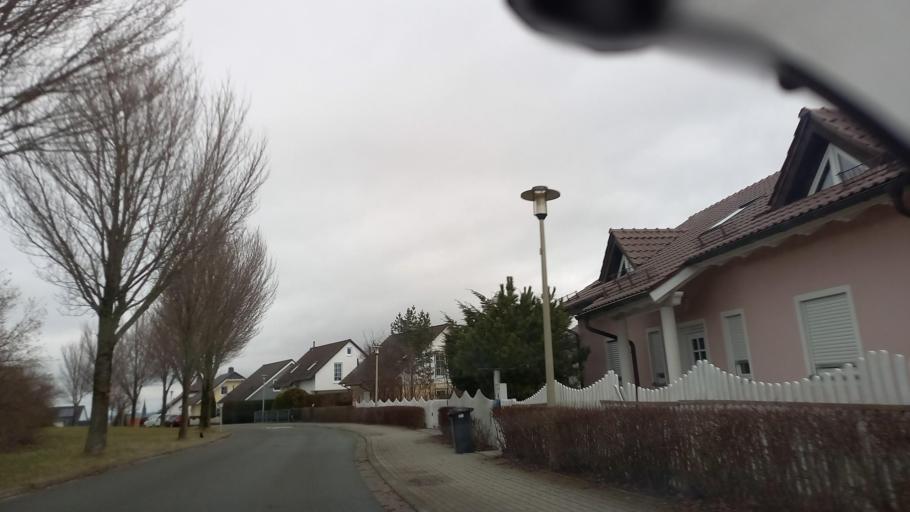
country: DE
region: Saxony
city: Lichtentanne
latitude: 50.6745
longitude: 12.4641
